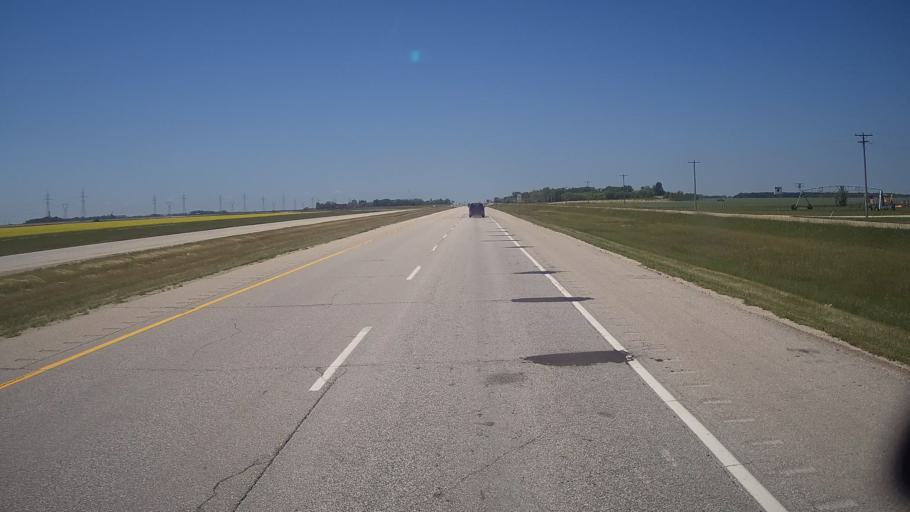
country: CA
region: Manitoba
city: Winnipeg
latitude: 49.9899
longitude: -97.2454
